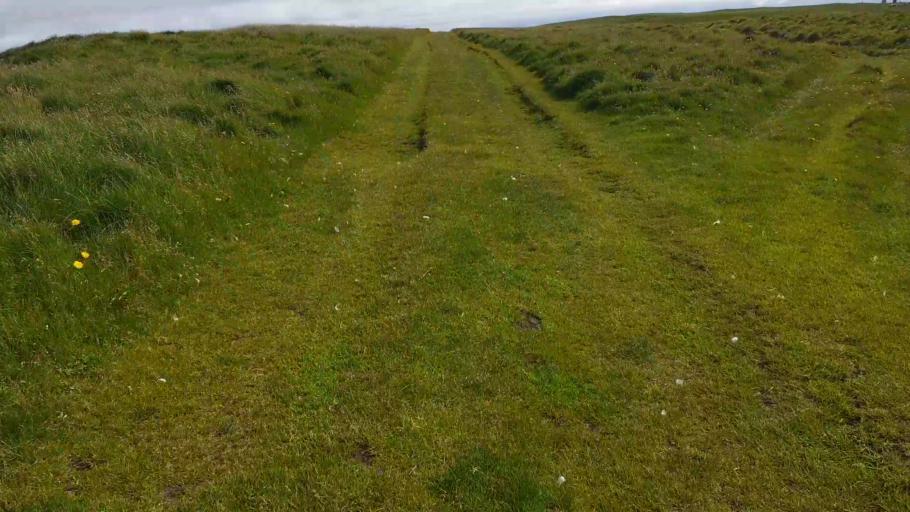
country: IS
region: Northeast
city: Dalvik
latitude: 66.5521
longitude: -17.9960
